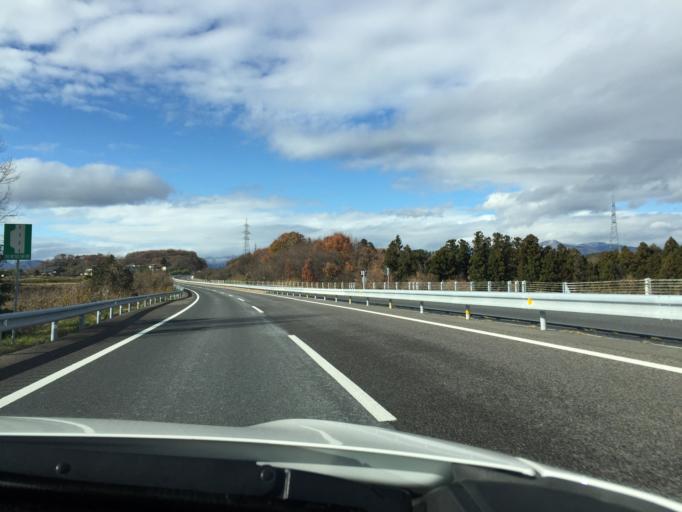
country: JP
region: Fukushima
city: Koriyama
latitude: 37.4553
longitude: 140.3989
